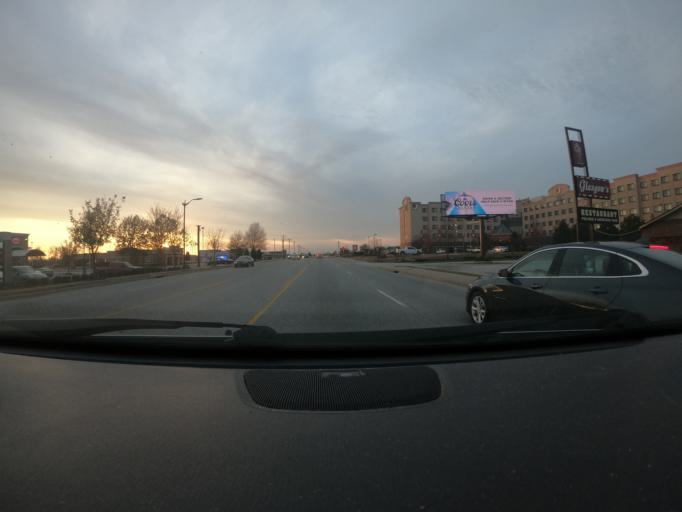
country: US
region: Arkansas
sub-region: Benton County
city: Bentonville
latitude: 36.3355
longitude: -94.2048
